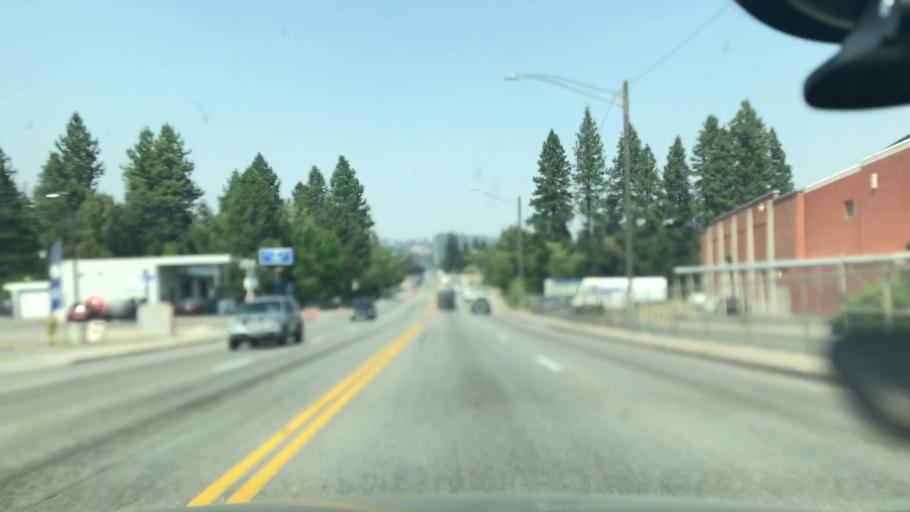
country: US
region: Washington
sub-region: Spokane County
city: Millwood
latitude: 47.6881
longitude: -117.2827
